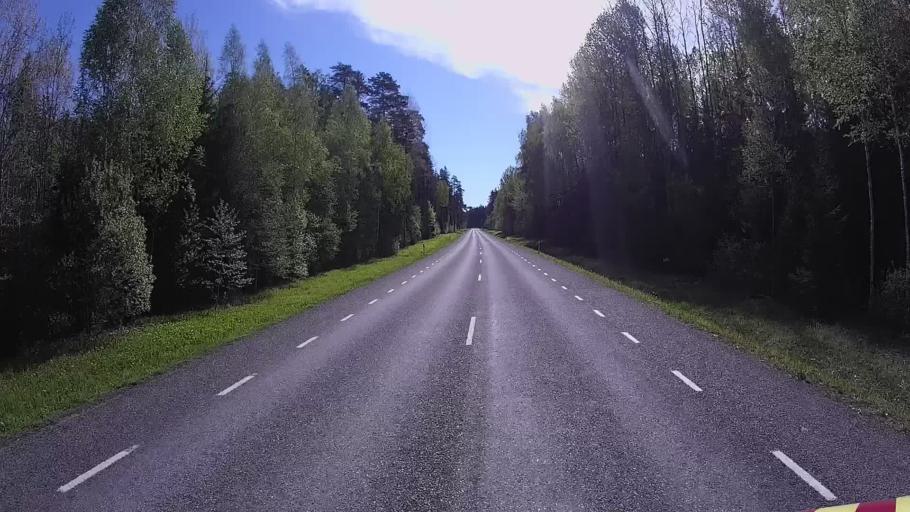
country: EE
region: Polvamaa
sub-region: Raepina vald
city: Rapina
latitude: 58.0986
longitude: 27.3902
